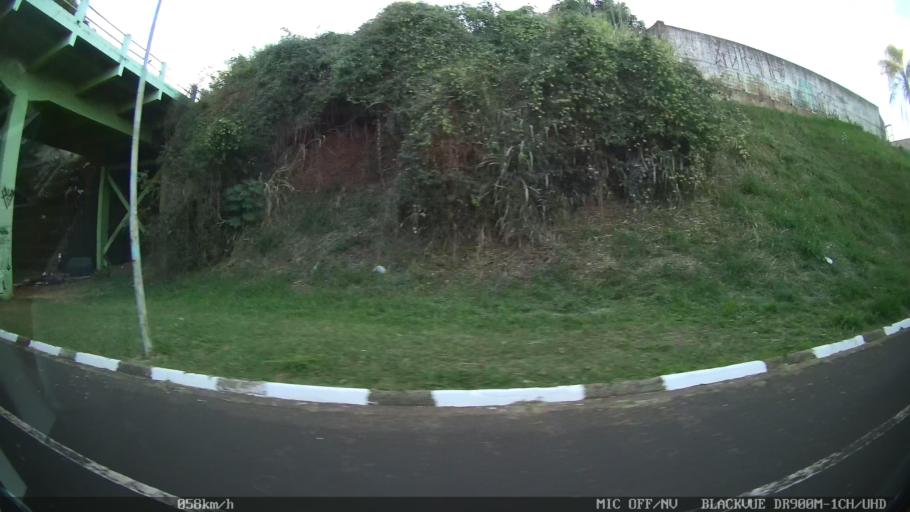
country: BR
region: Sao Paulo
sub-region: Franca
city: Franca
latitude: -20.5358
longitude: -47.4067
